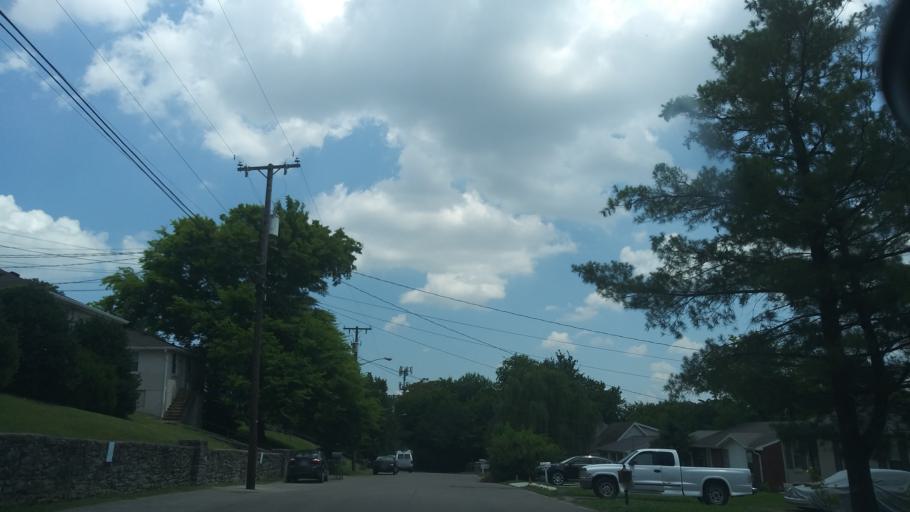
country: US
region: Tennessee
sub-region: Davidson County
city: Nashville
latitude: 36.1486
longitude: -86.8261
